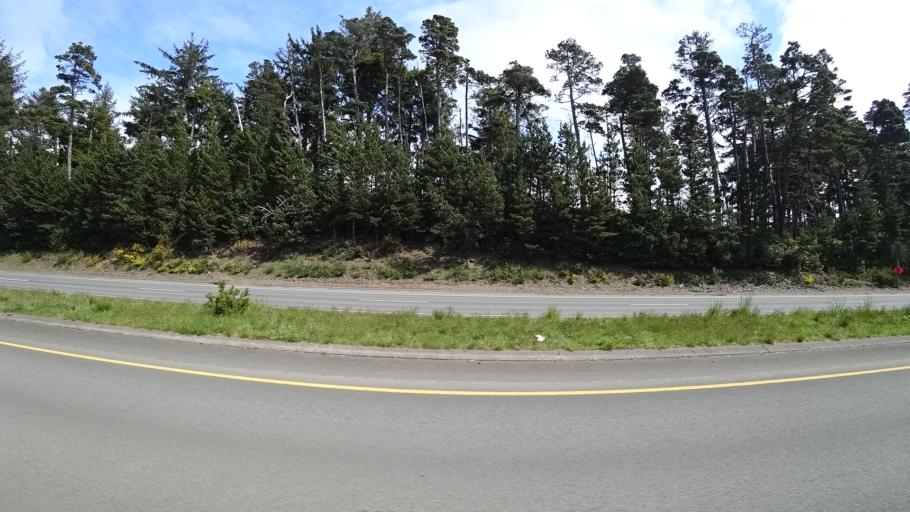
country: US
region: Oregon
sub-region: Lincoln County
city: Lincoln Beach
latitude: 44.8583
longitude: -124.0398
